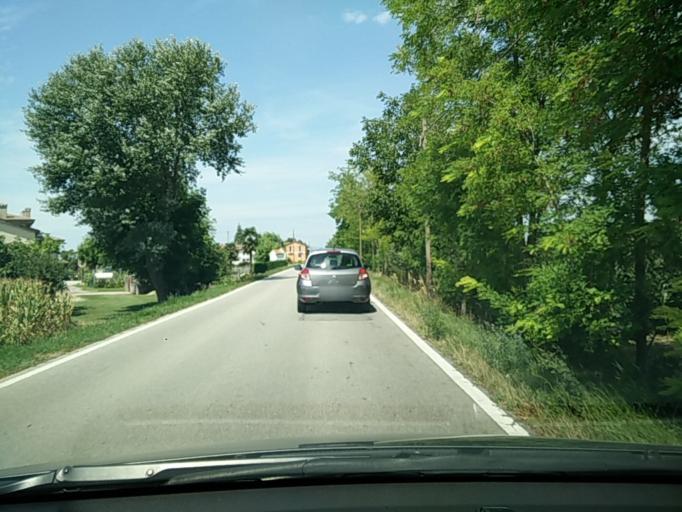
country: IT
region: Veneto
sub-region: Provincia di Venezia
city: Passarella
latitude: 45.5759
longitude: 12.6134
